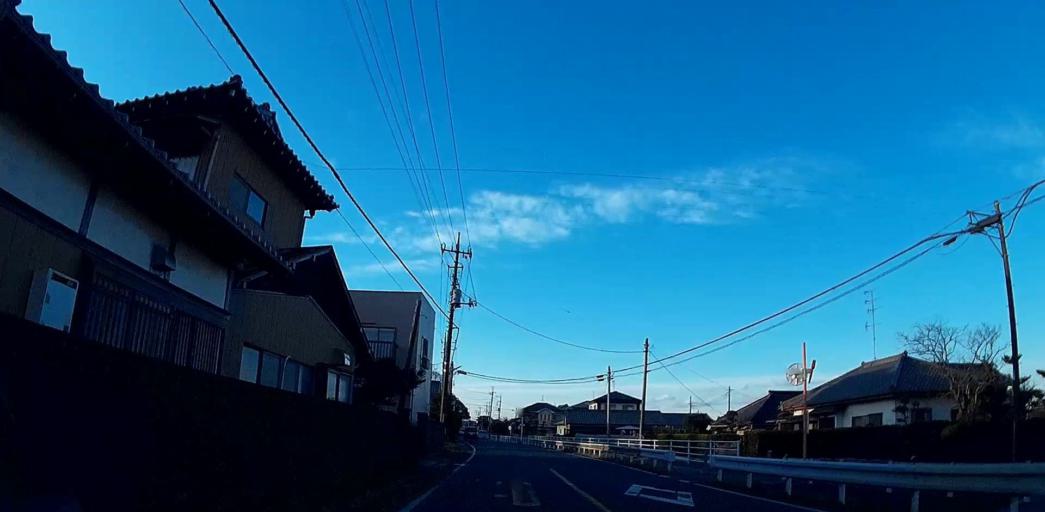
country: JP
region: Chiba
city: Omigawa
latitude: 35.8737
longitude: 140.5894
